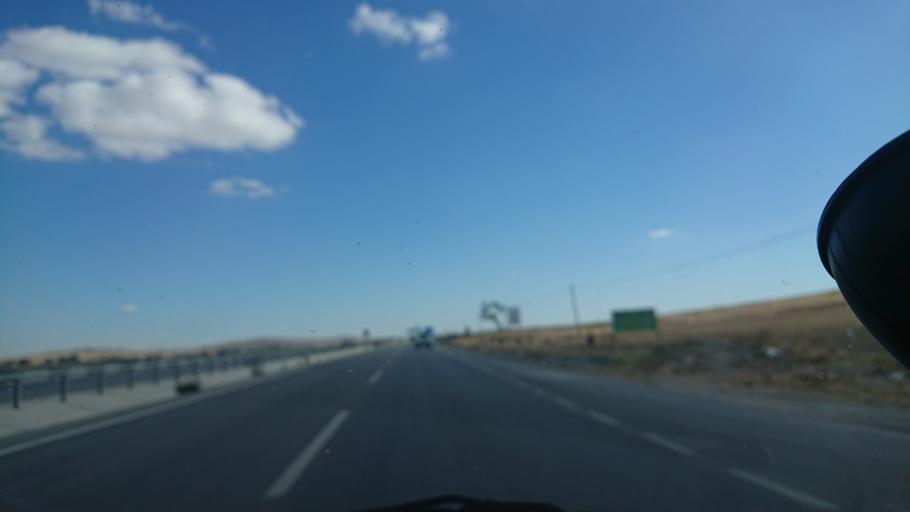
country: TR
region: Eskisehir
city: Mahmudiye
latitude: 39.5239
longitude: 30.9564
